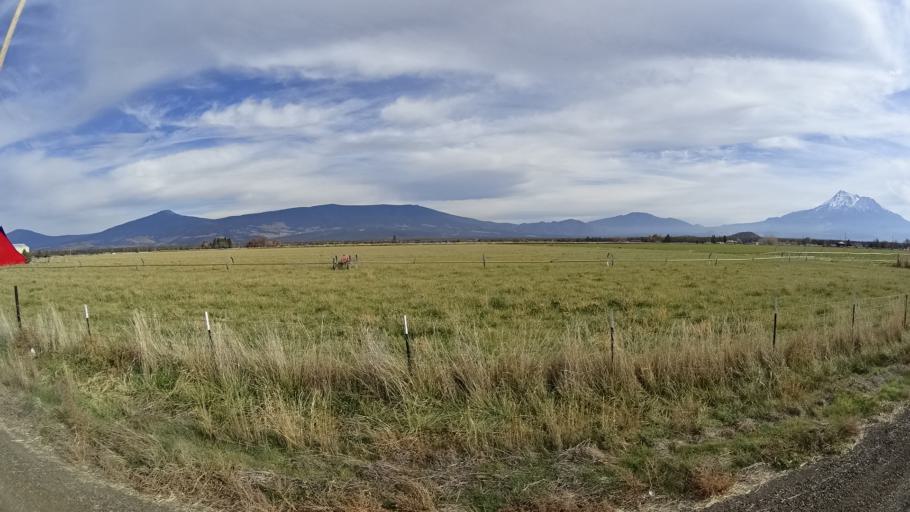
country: US
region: California
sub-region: Siskiyou County
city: Montague
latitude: 41.6206
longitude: -122.3997
